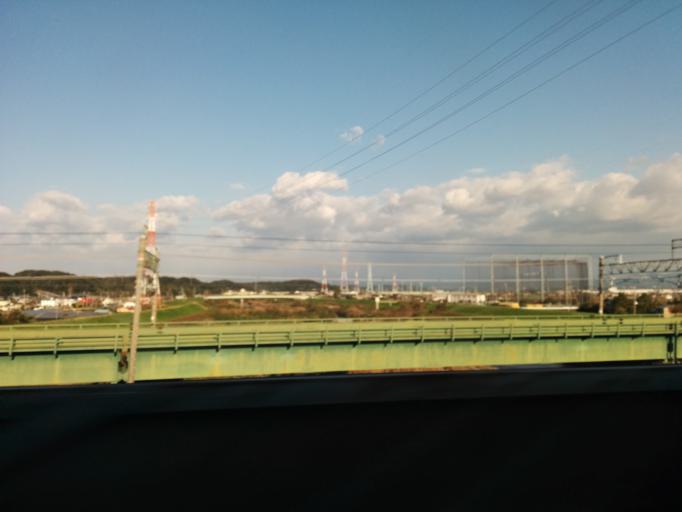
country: JP
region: Shizuoka
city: Fukuroi
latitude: 34.7251
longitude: 137.8955
